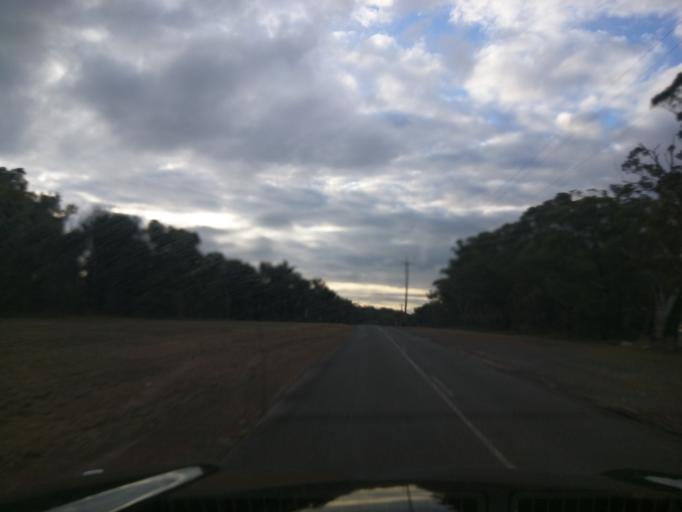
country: AU
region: New South Wales
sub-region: Wollondilly
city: Douglas Park
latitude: -34.3129
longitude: 150.7396
